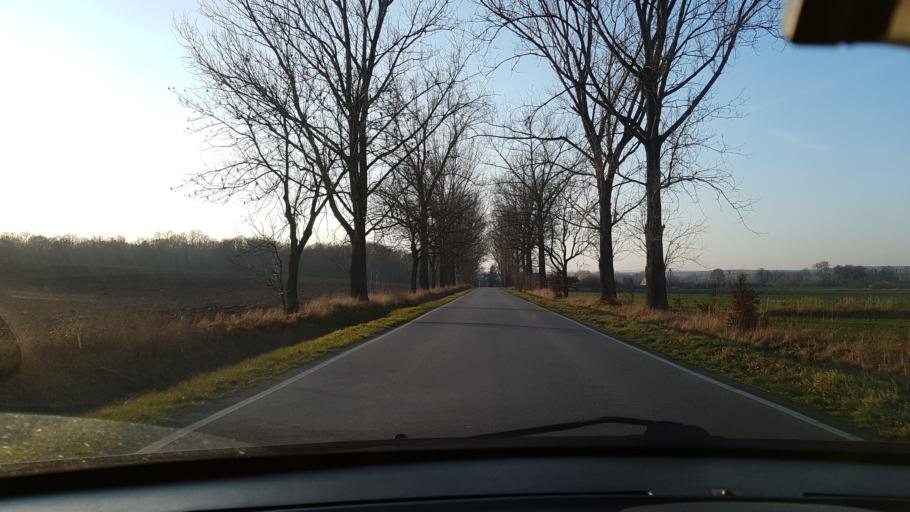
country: PL
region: Lower Silesian Voivodeship
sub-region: Powiat zabkowicki
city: Henrykow
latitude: 50.6588
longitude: 17.0395
